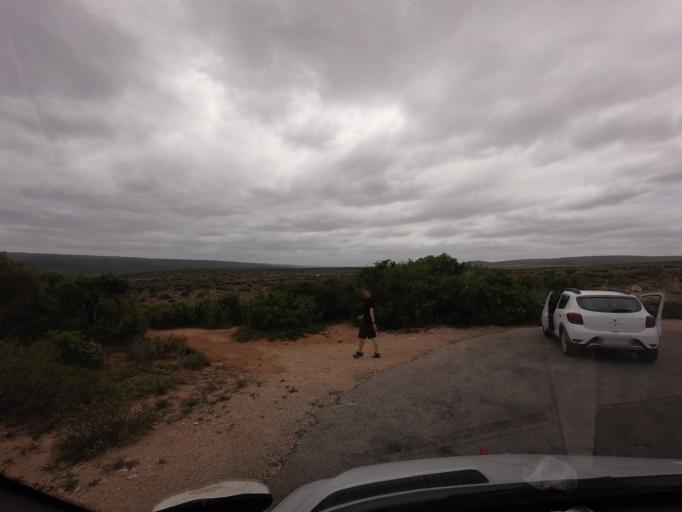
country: ZA
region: Eastern Cape
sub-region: Cacadu District Municipality
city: Kirkwood
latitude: -33.4402
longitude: 25.7826
